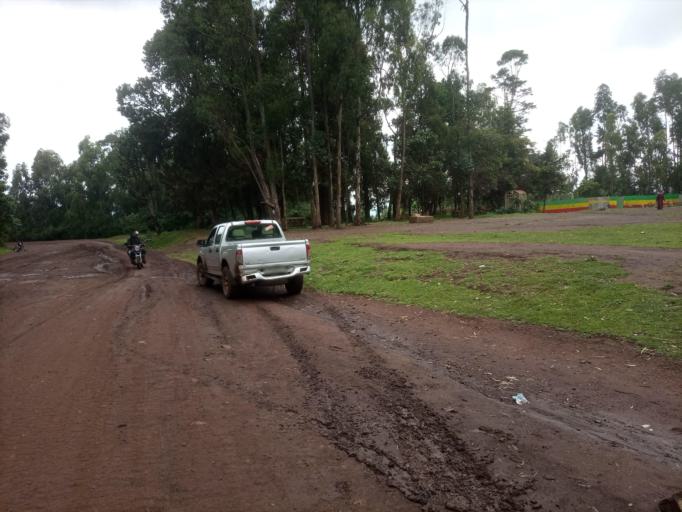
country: ET
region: Southern Nations, Nationalities, and People's Region
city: K'olito
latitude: 7.3538
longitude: 37.9446
